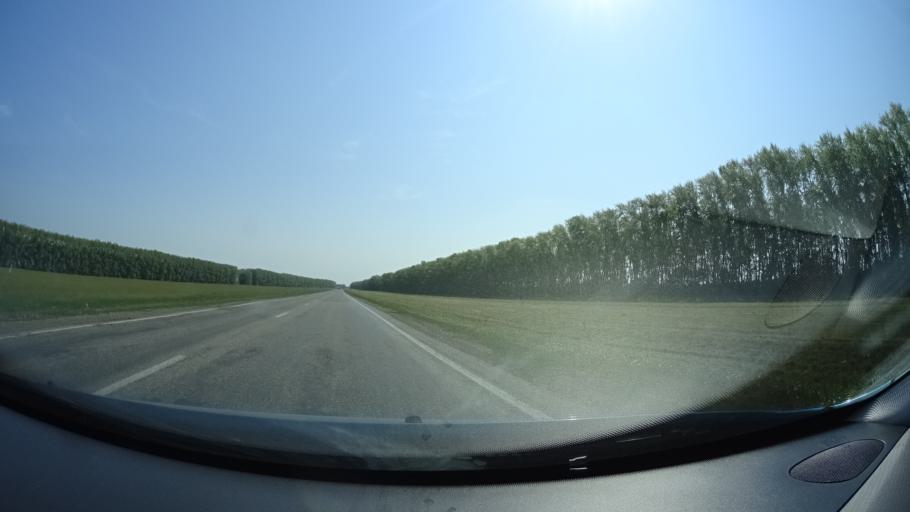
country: RU
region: Bashkortostan
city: Karmaskaly
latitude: 54.3964
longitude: 56.1057
